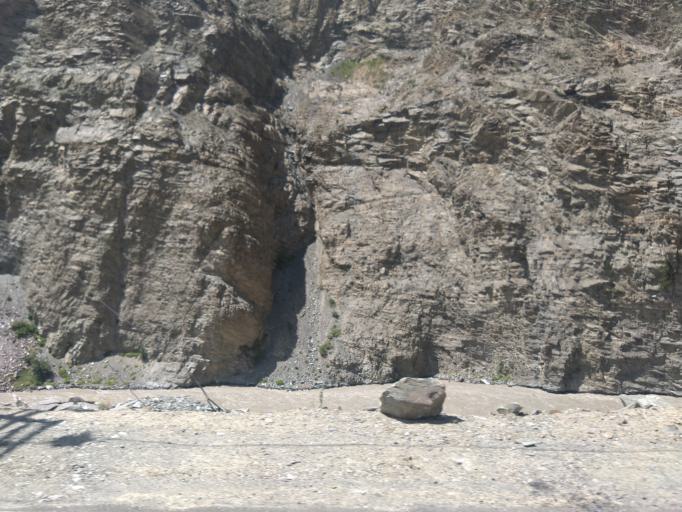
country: CN
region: Tibet Autonomous Region
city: Diyag
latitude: 31.6857
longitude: 78.4976
